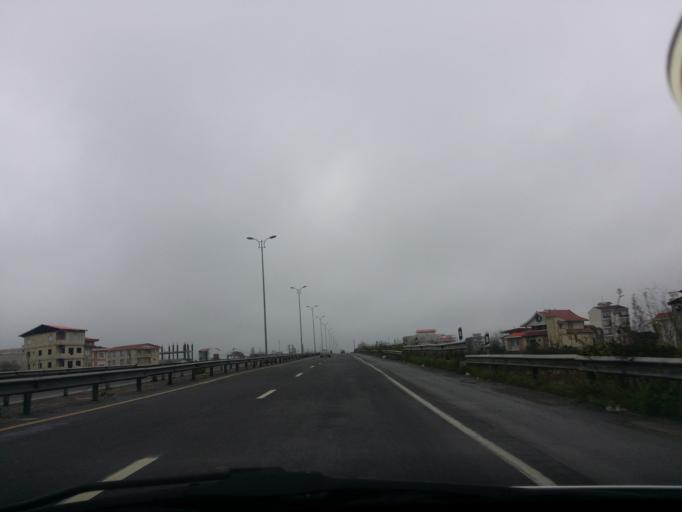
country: IR
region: Mazandaran
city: Tonekabon
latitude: 36.8052
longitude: 50.8746
